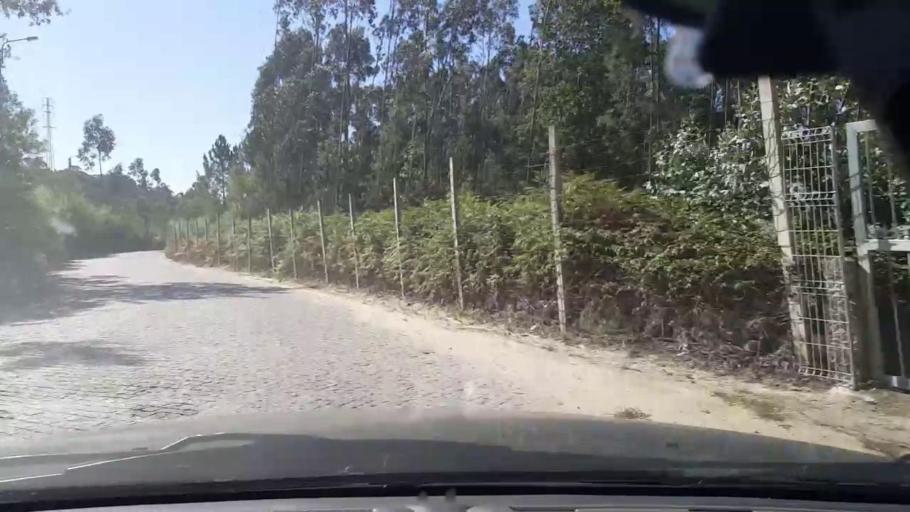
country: PT
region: Porto
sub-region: Maia
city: Gemunde
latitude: 41.2975
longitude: -8.6652
